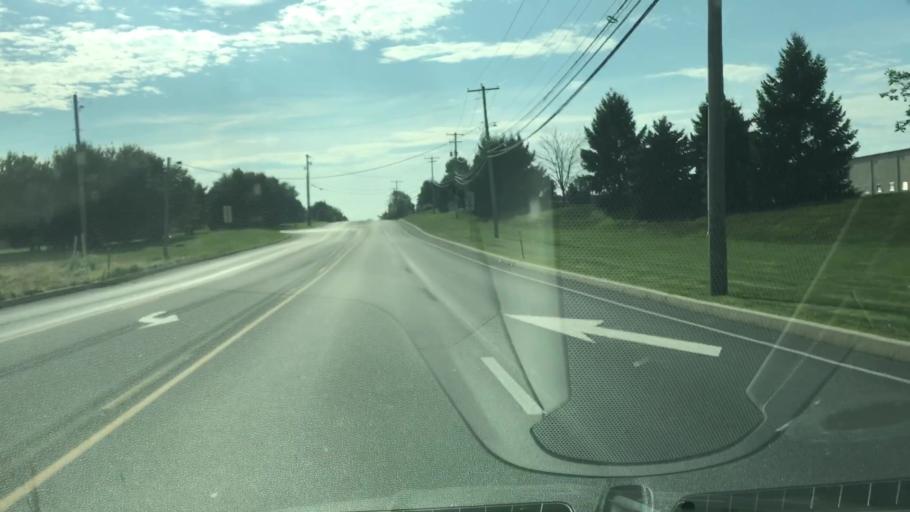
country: US
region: Pennsylvania
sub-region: Dauphin County
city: Middletown
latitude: 40.2300
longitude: -76.7413
